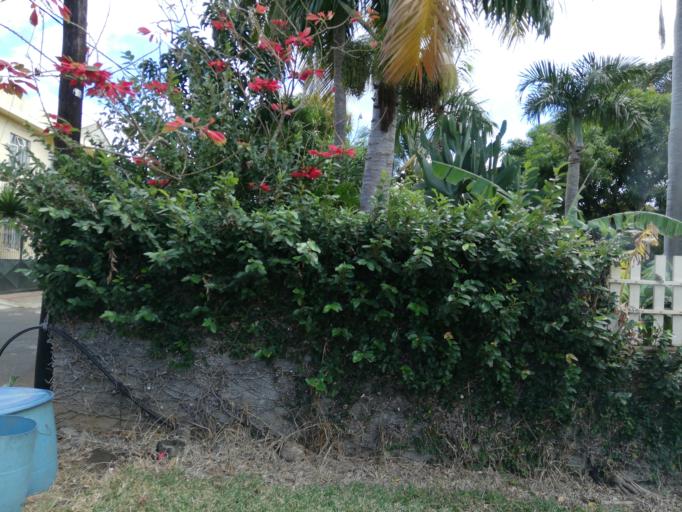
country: MU
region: Moka
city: Pailles
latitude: -20.1941
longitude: 57.4727
